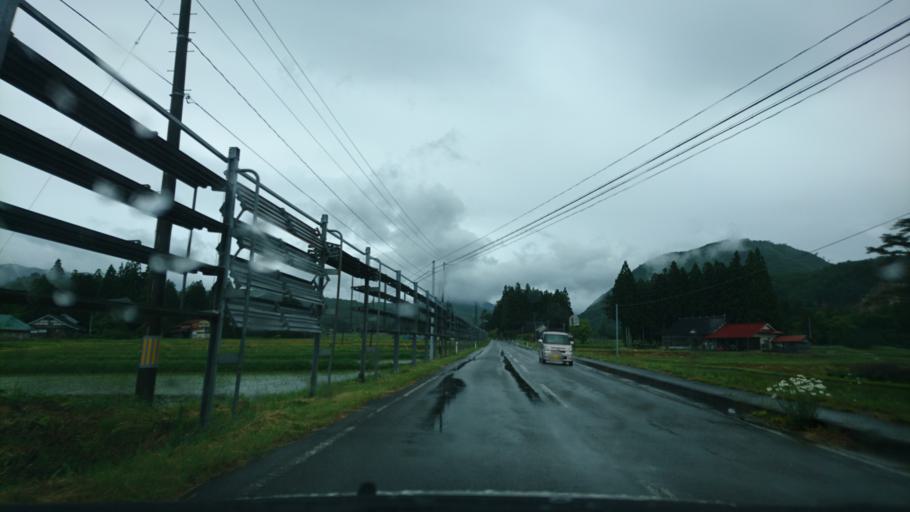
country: JP
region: Iwate
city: Ichinoseki
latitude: 38.9768
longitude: 140.9247
